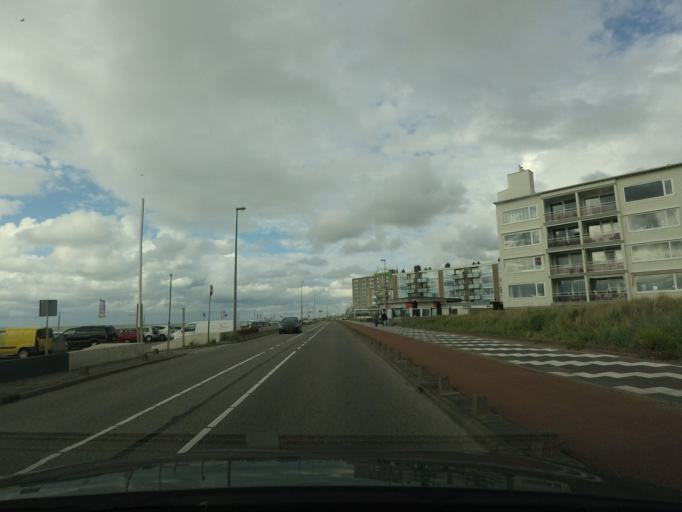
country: NL
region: North Holland
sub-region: Gemeente Zandvoort
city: Zandvoort
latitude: 52.3780
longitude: 4.5288
